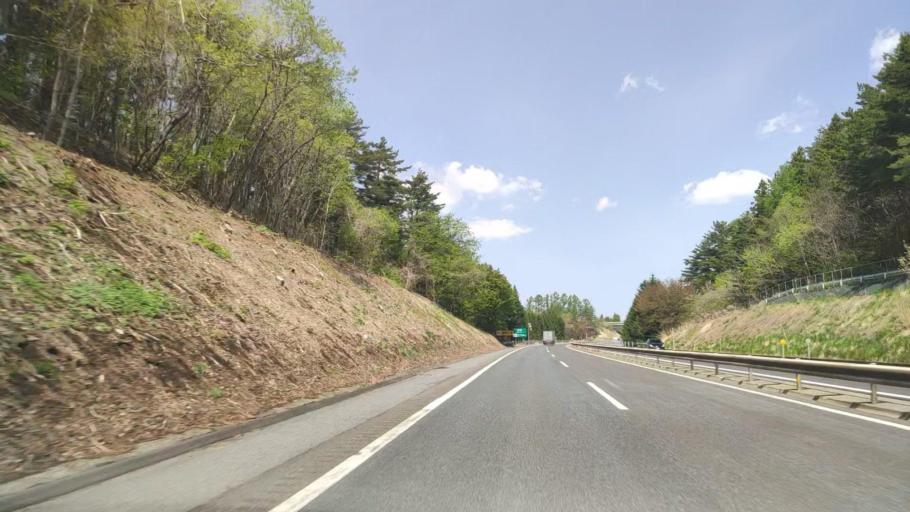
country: JP
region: Aomori
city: Hachinohe
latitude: 40.3990
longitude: 141.4461
